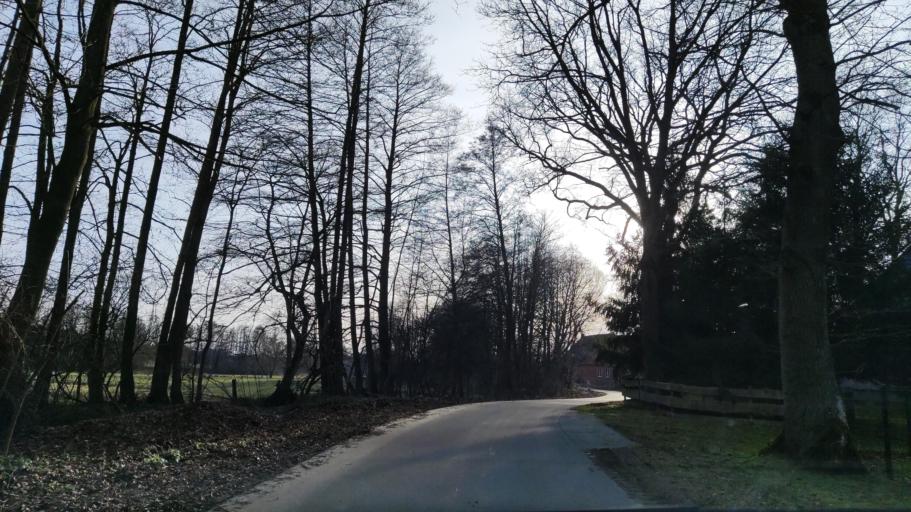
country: DE
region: Schleswig-Holstein
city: Langenlehsten
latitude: 53.4617
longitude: 10.7741
